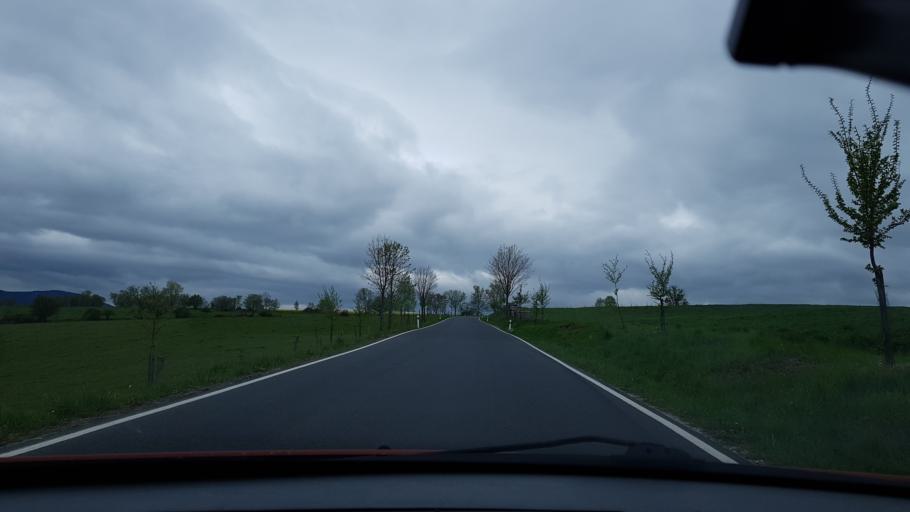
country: CZ
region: Olomoucky
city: Mikulovice
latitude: 50.3086
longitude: 17.3163
